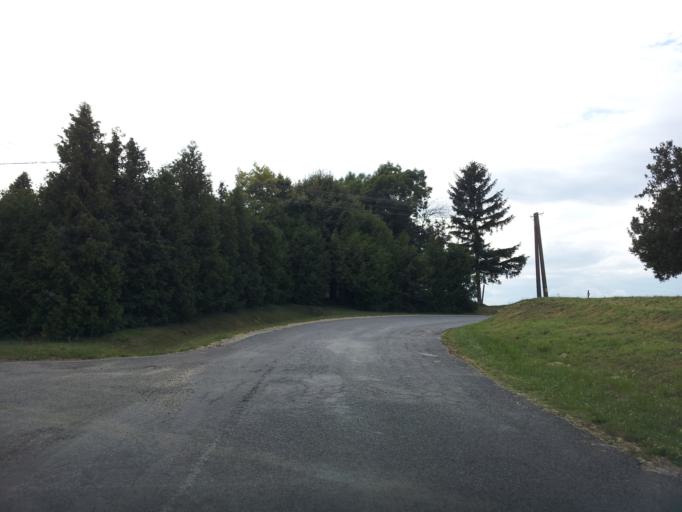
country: HU
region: Vas
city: Janoshaza
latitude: 47.1252
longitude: 17.1115
